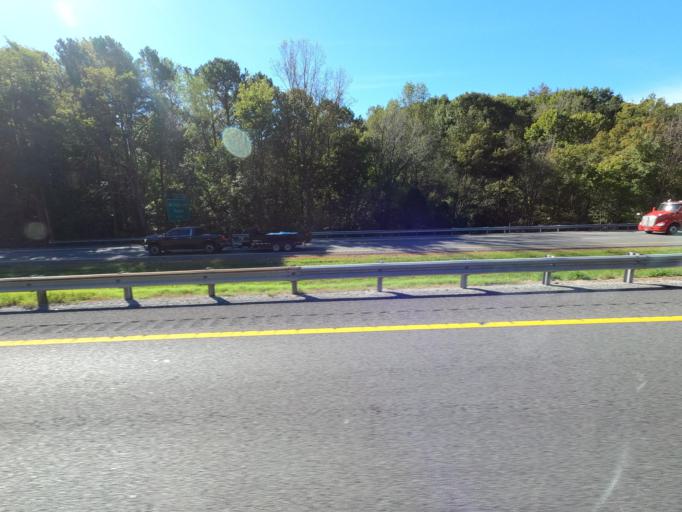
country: US
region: Tennessee
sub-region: Cheatham County
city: Pegram
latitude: 36.0775
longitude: -87.0320
